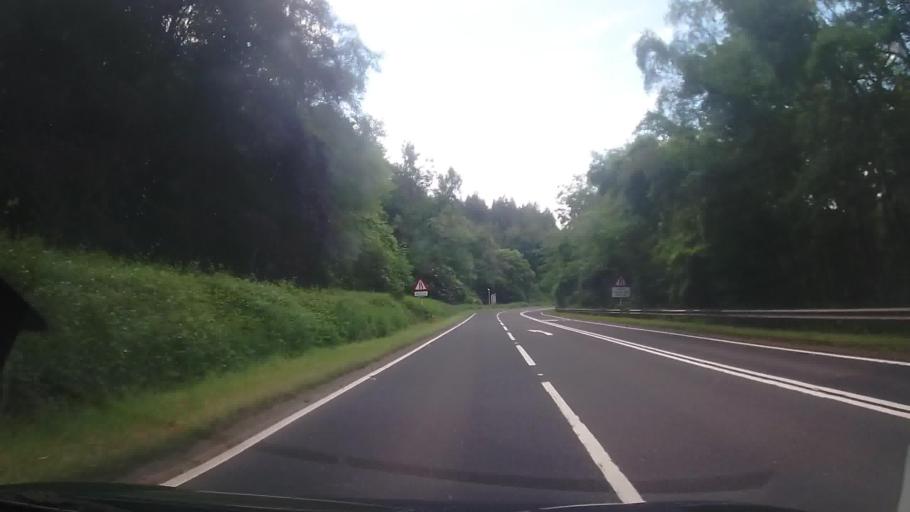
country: GB
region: England
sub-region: Herefordshire
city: Hope under Dinmore
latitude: 52.1564
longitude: -2.7192
